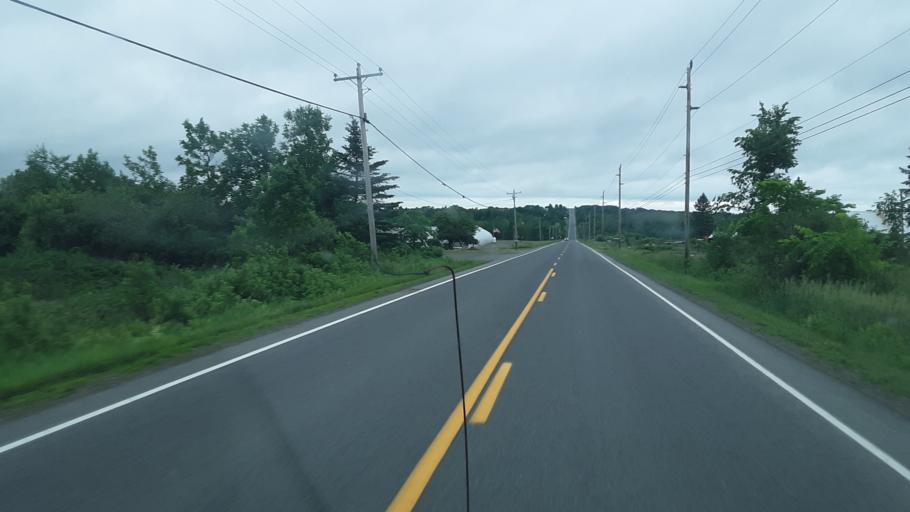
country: US
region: Maine
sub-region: Penobscot County
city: Patten
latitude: 45.9717
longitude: -68.4507
